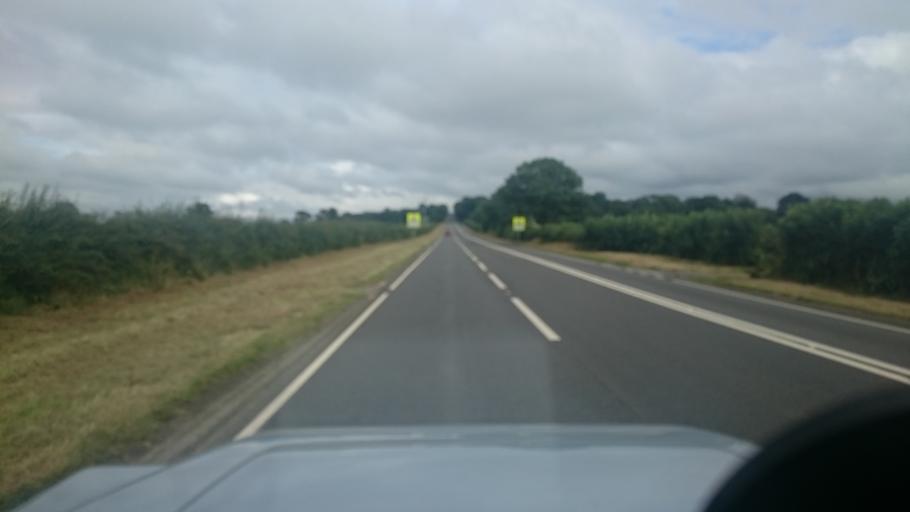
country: GB
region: Wales
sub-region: Pembrokeshire
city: Wiston
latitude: 51.8051
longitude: -4.9013
